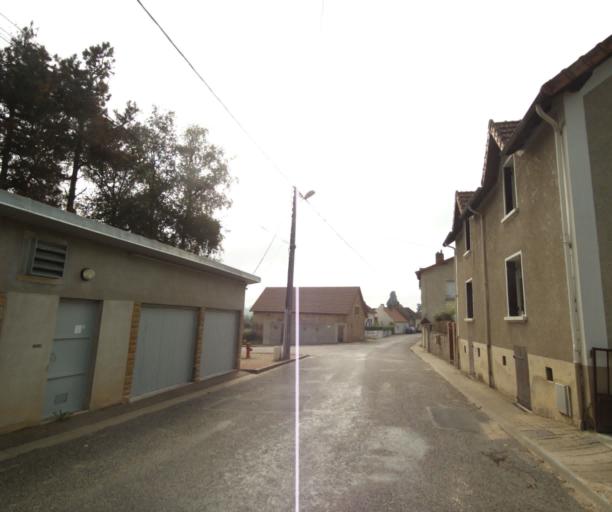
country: FR
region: Bourgogne
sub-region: Departement de Saone-et-Loire
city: Charolles
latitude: 46.4355
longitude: 4.2683
